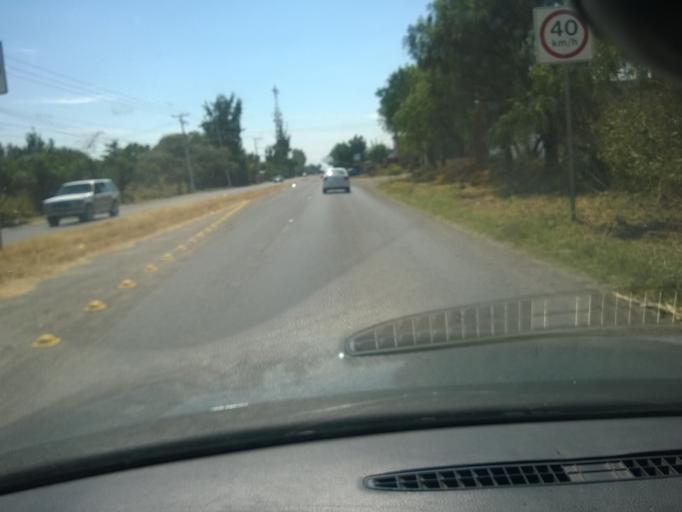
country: MX
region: Guanajuato
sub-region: Leon
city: El CERESO
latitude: 20.9818
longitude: -101.7018
